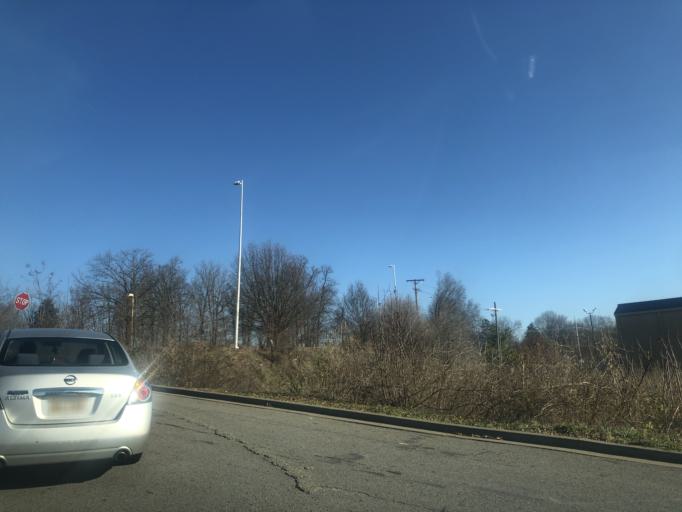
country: US
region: Tennessee
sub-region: Rutherford County
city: La Vergne
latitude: 36.0446
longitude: -86.6493
